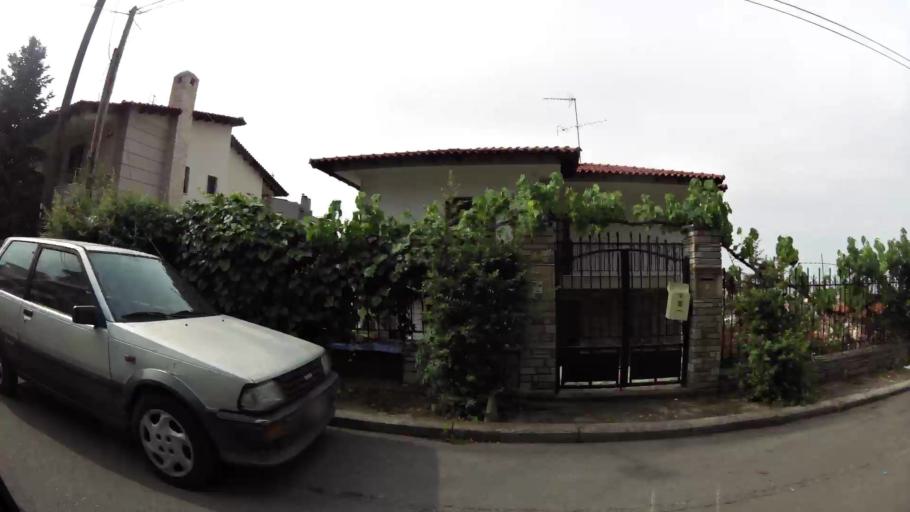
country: GR
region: Central Macedonia
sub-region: Nomos Thessalonikis
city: Panorama
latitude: 40.5847
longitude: 23.0306
